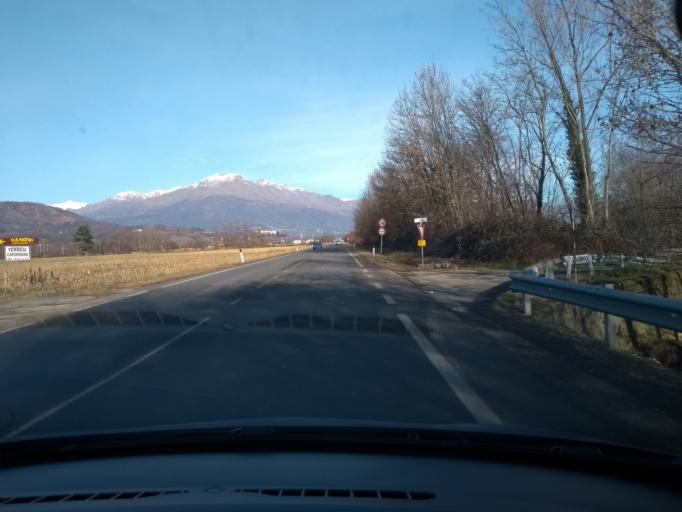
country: IT
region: Piedmont
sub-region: Provincia di Torino
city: Busano
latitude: 45.3408
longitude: 7.6555
